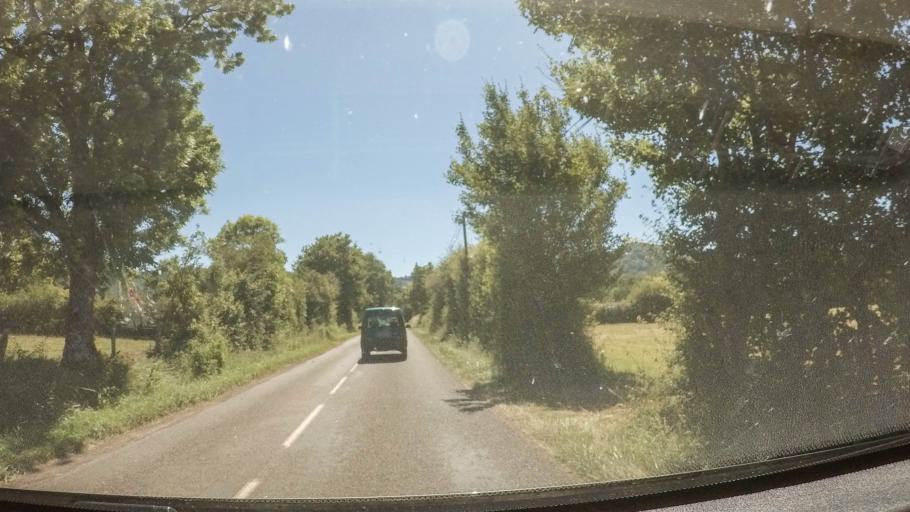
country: FR
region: Midi-Pyrenees
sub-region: Departement de l'Aveyron
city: Saint-Christophe-Vallon
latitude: 44.4630
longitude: 2.3974
